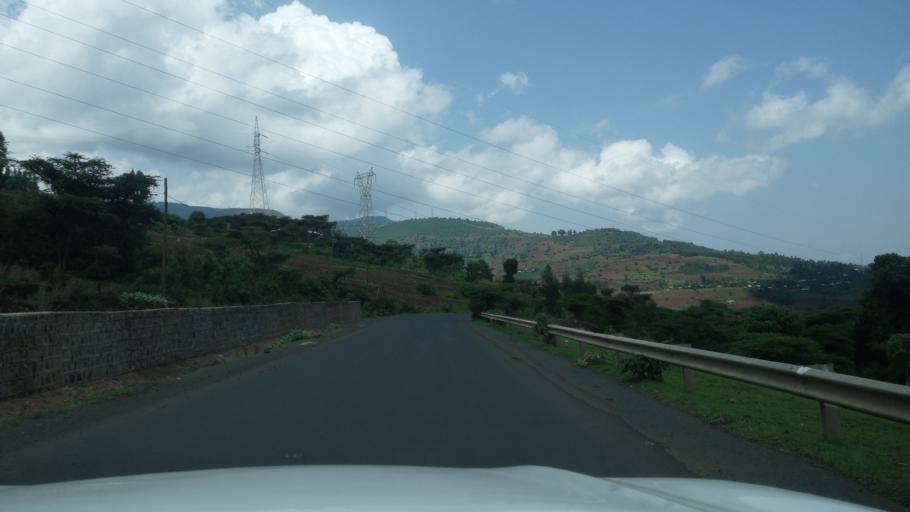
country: ET
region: Oromiya
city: Guder
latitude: 8.9889
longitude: 37.6095
